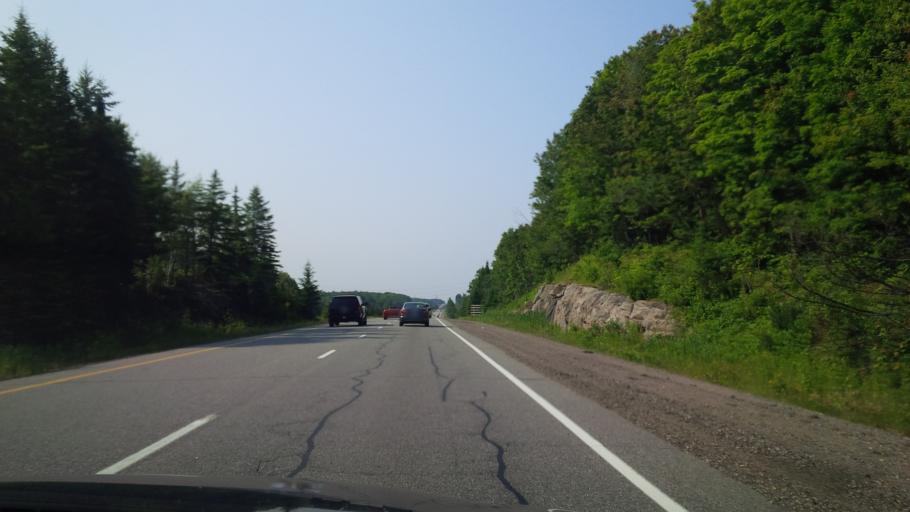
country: CA
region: Ontario
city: Bracebridge
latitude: 45.1883
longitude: -79.3130
